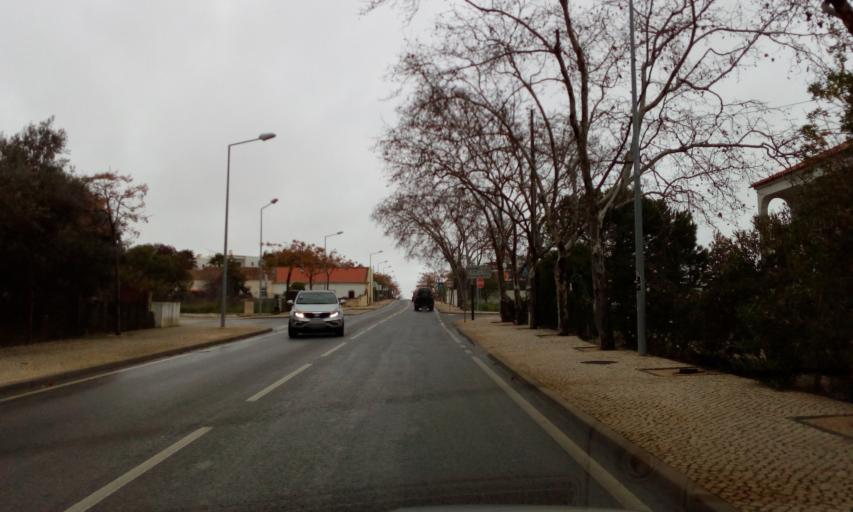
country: PT
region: Faro
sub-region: Albufeira
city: Ferreiras
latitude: 37.1274
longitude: -8.2456
